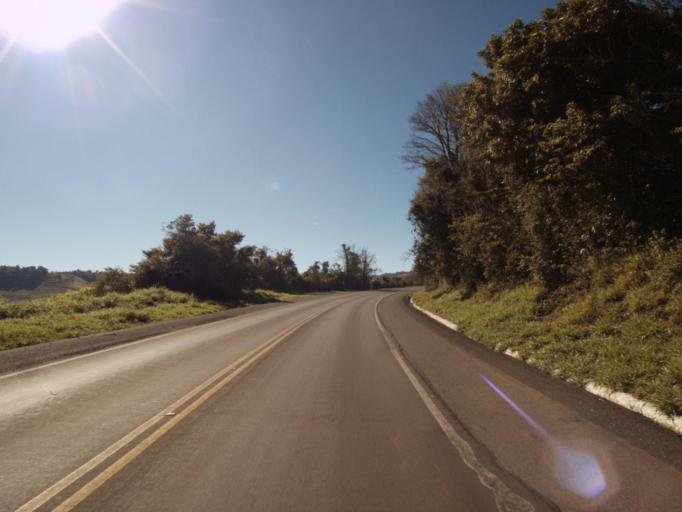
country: BR
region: Rio Grande do Sul
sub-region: Frederico Westphalen
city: Frederico Westphalen
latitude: -26.7975
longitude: -53.3266
